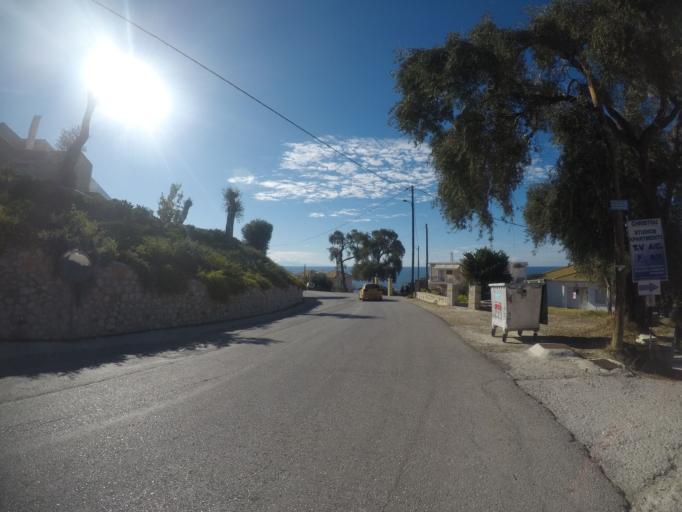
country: GR
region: Epirus
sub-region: Nomos Prevezis
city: Parga
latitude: 39.2883
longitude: 20.3939
